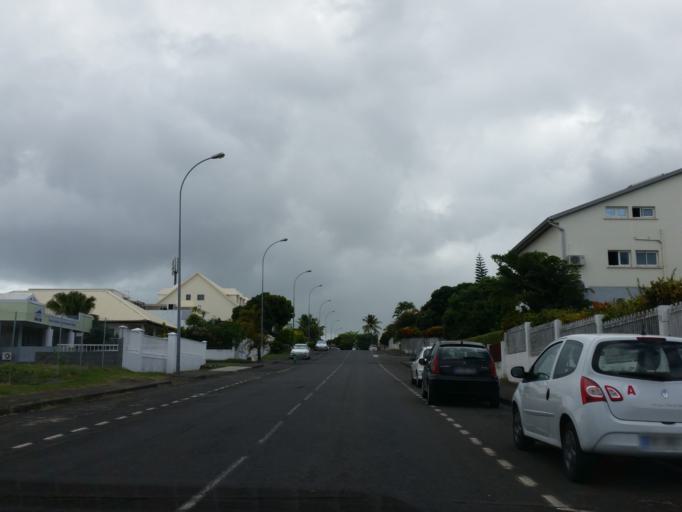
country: RE
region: Reunion
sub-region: Reunion
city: Saint-Denis
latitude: -20.9034
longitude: 55.4897
